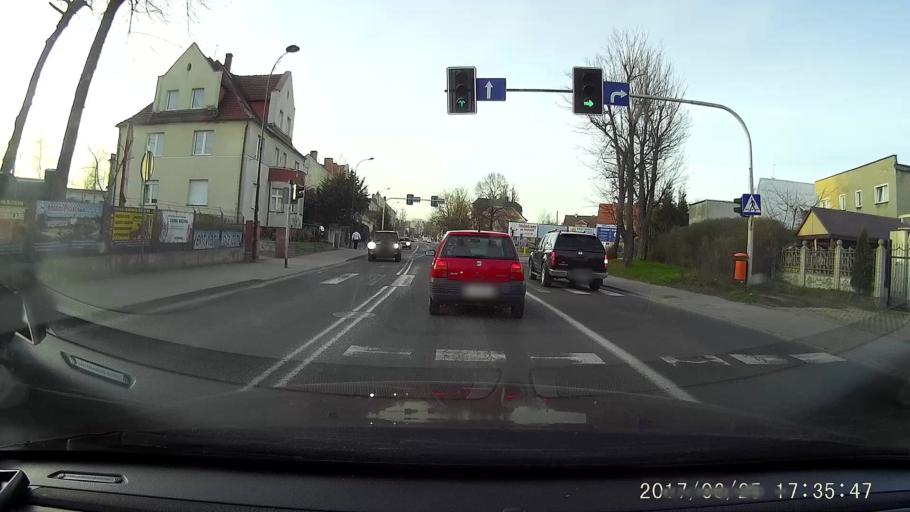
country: PL
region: Lower Silesian Voivodeship
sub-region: Powiat zgorzelecki
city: Zgorzelec
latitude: 51.1351
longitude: 15.0150
